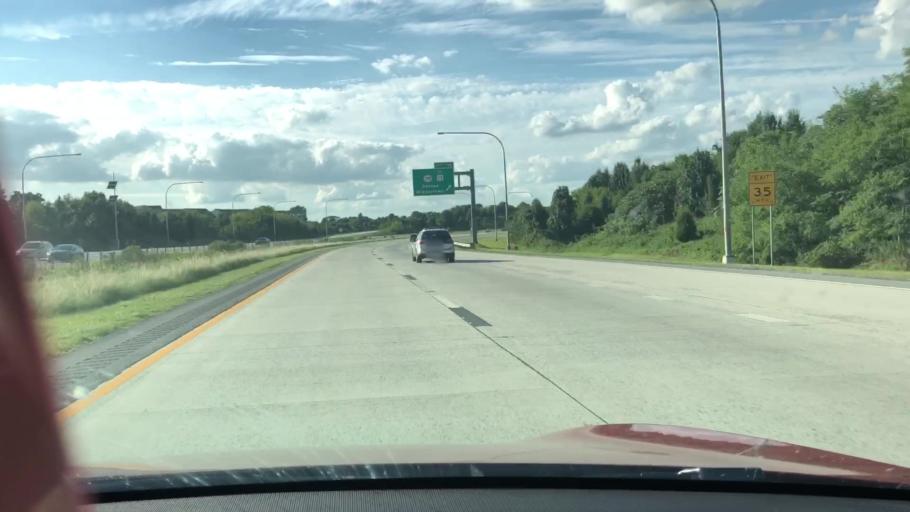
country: US
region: Delaware
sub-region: New Castle County
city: Middletown
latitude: 39.4488
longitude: -75.6721
